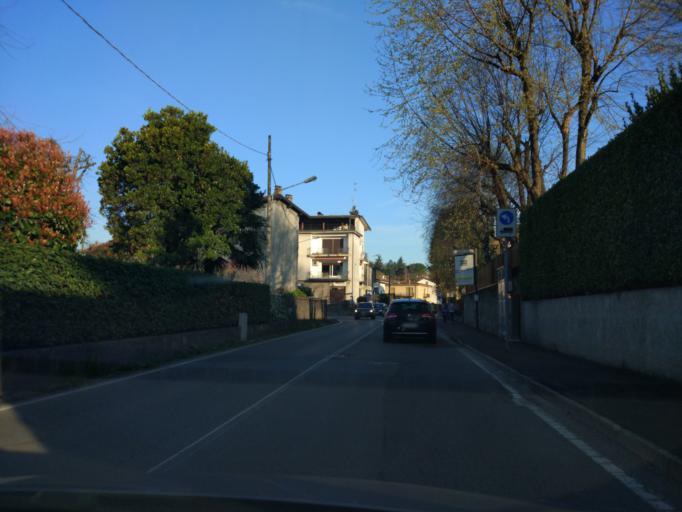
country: IT
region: Lombardy
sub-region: Provincia di Como
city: Cantu
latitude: 45.7457
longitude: 9.1213
